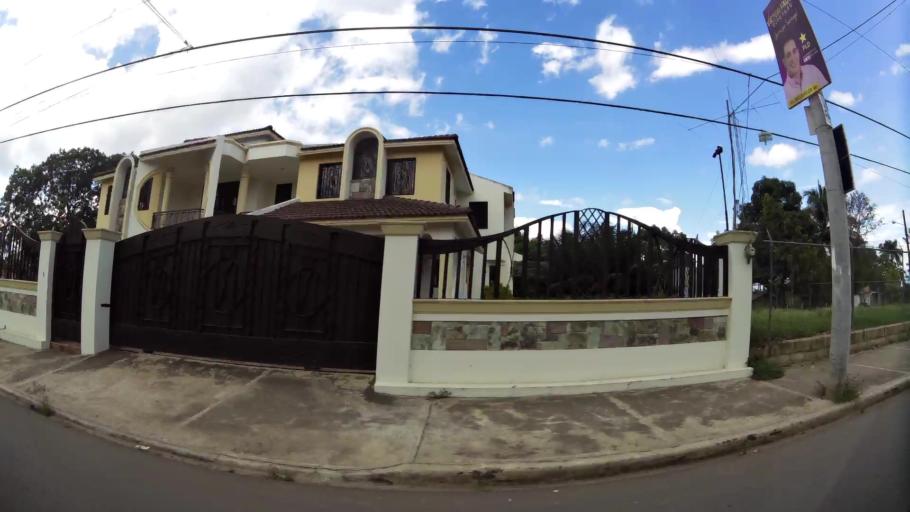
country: DO
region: Santiago
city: Licey al Medio
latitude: 19.3923
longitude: -70.6416
